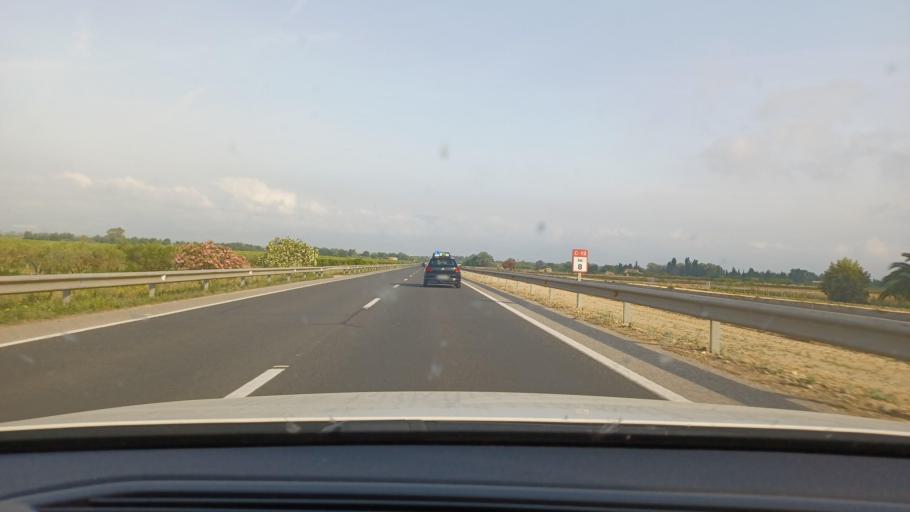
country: ES
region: Catalonia
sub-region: Provincia de Tarragona
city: Masdenverge
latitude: 40.7484
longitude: 0.5547
